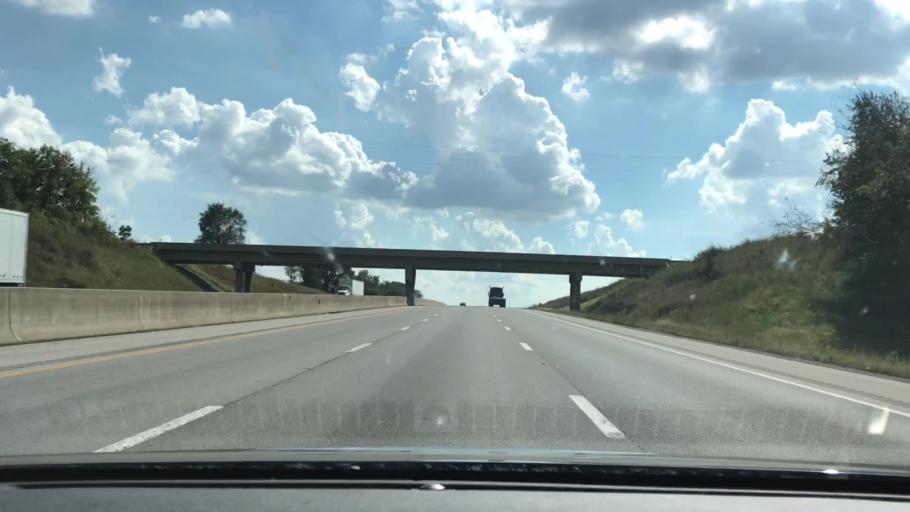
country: US
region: Kentucky
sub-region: Warren County
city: Plano
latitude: 36.7960
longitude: -86.4749
